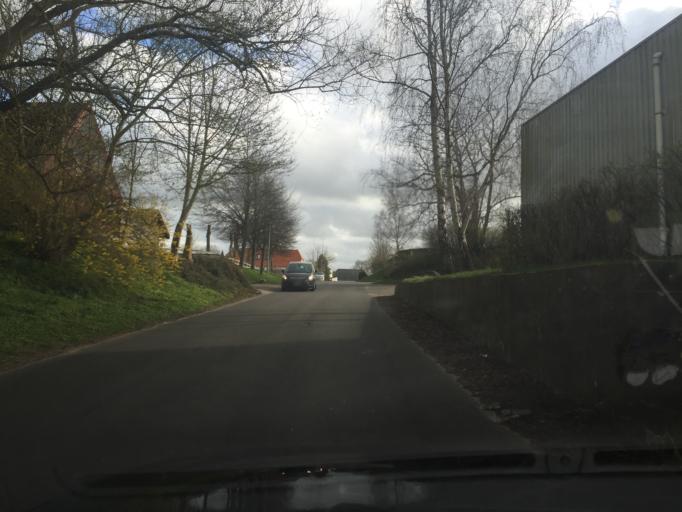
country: DK
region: South Denmark
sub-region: Kolding Kommune
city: Sonder Bjert
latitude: 55.4634
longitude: 9.5593
